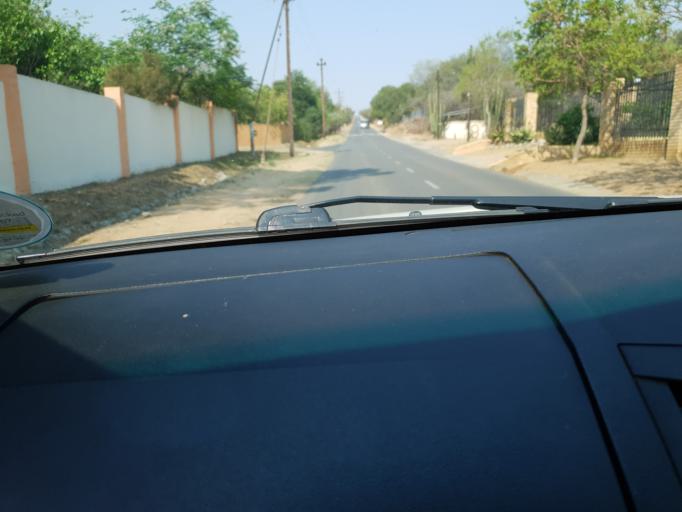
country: ZA
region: Gauteng
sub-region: City of Johannesburg Metropolitan Municipality
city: Midrand
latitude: -25.9902
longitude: 28.0986
